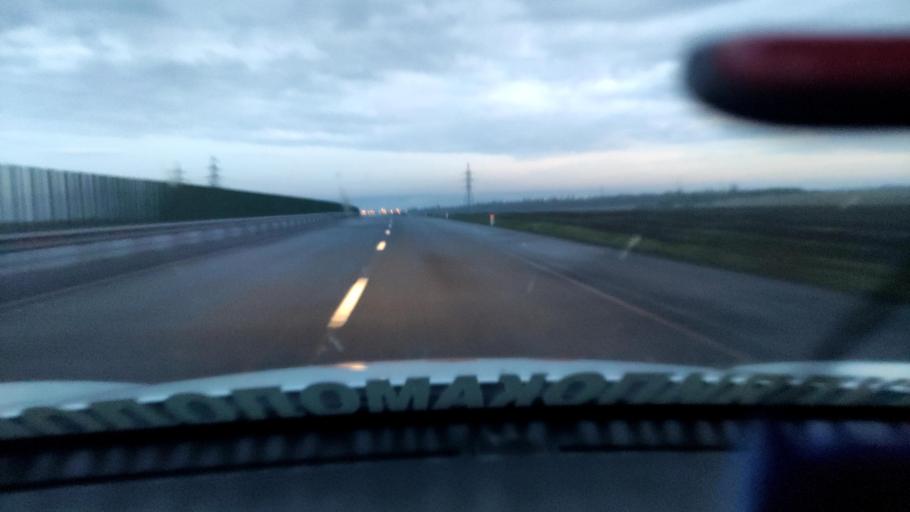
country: RU
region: Rostov
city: Tarasovskiy
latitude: 48.7452
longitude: 40.3899
